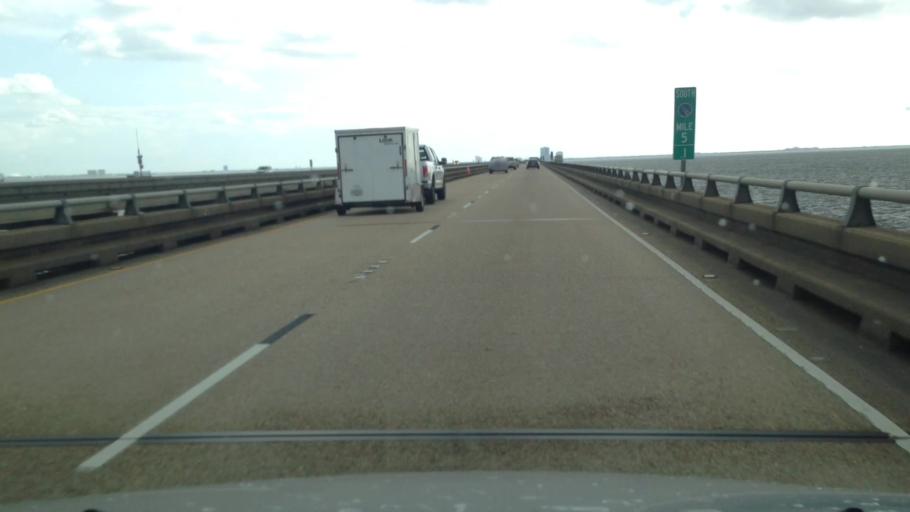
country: US
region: Louisiana
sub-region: Jefferson Parish
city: Metairie
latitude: 30.0951
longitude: -90.1413
